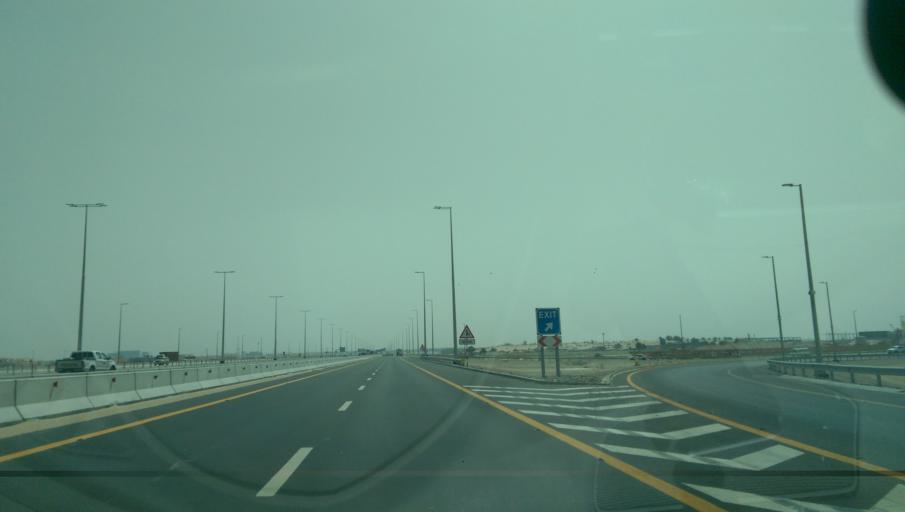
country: AE
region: Abu Dhabi
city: Abu Dhabi
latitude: 24.2962
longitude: 54.5776
